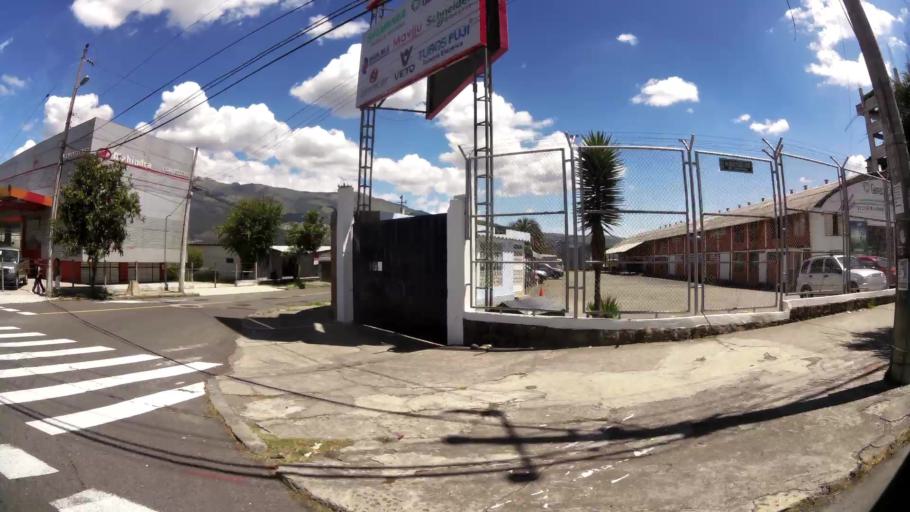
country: EC
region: Pichincha
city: Quito
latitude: -0.1241
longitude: -78.4807
